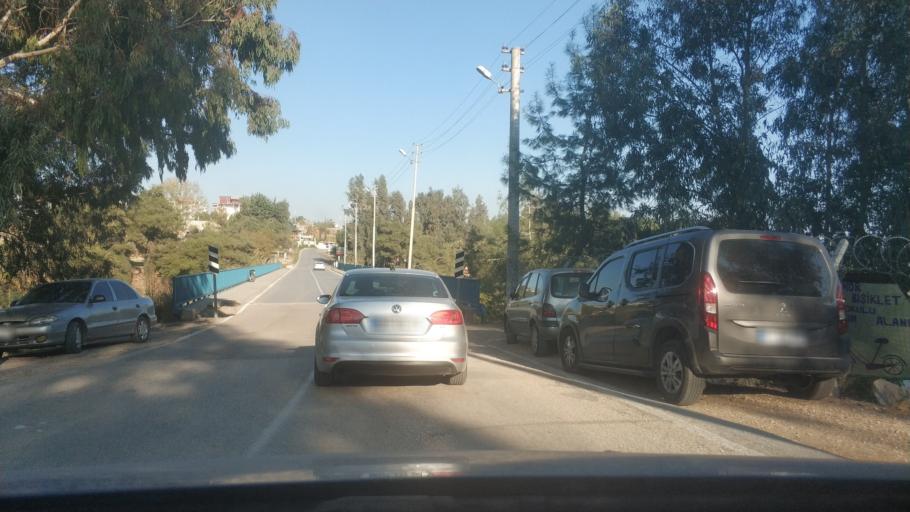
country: TR
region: Adana
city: Adana
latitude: 37.1043
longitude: 35.2949
